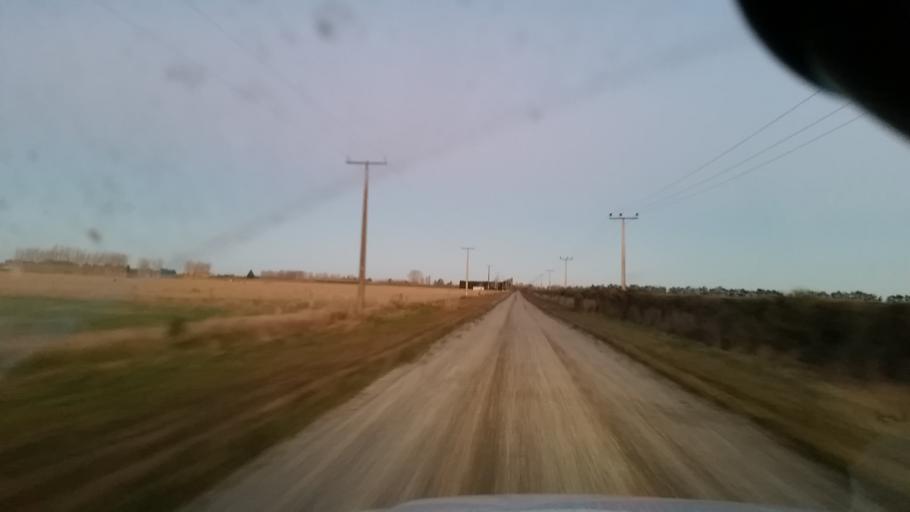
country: NZ
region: Canterbury
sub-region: Ashburton District
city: Tinwald
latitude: -43.9925
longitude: 171.6593
